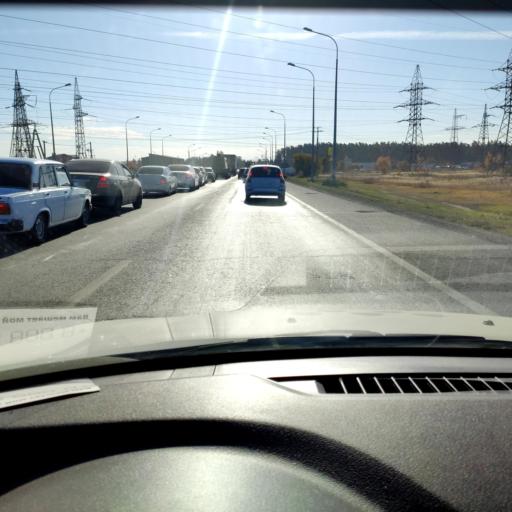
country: RU
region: Samara
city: Zhigulevsk
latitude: 53.5443
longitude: 49.5124
